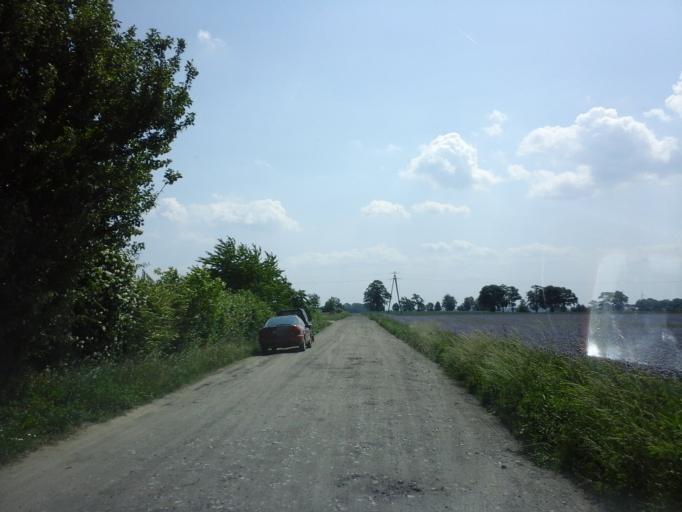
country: PL
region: West Pomeranian Voivodeship
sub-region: Powiat choszczenski
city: Choszczno
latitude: 53.1551
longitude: 15.3990
